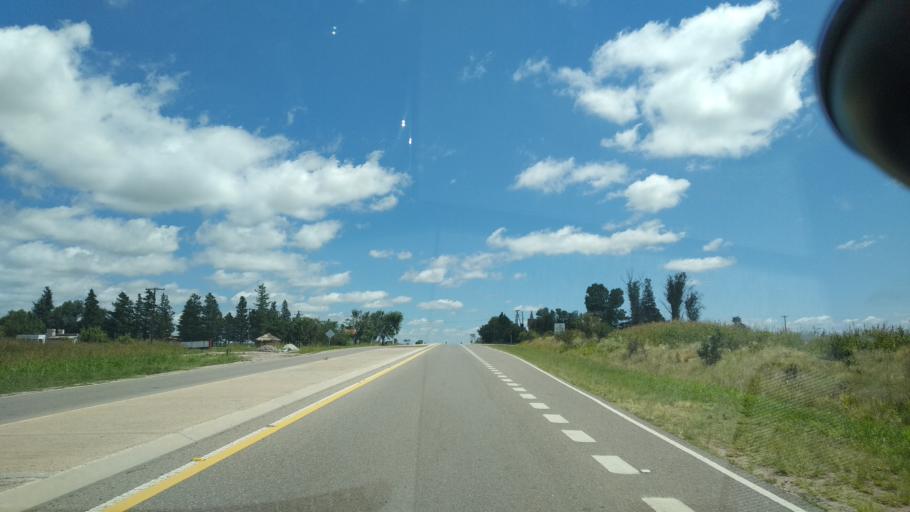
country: AR
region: Cordoba
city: Villa Cura Brochero
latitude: -31.6568
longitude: -65.0987
